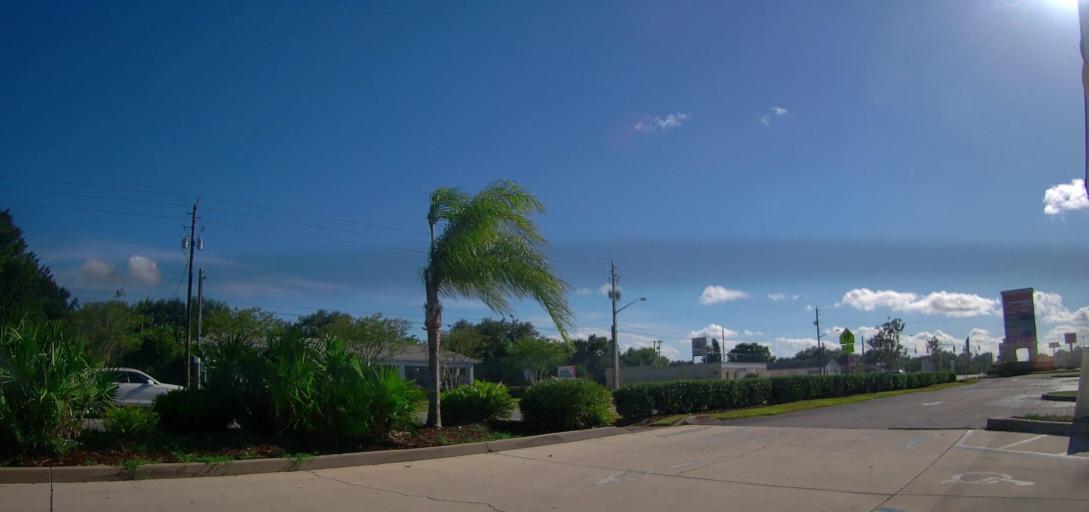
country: US
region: Florida
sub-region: Brevard County
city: Titusville
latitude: 28.5570
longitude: -80.8093
